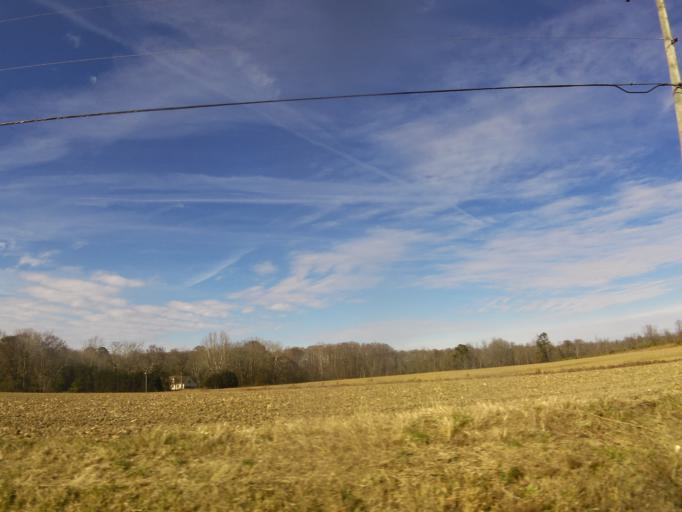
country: US
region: Virginia
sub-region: Isle of Wight County
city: Windsor
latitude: 36.7769
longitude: -76.8415
